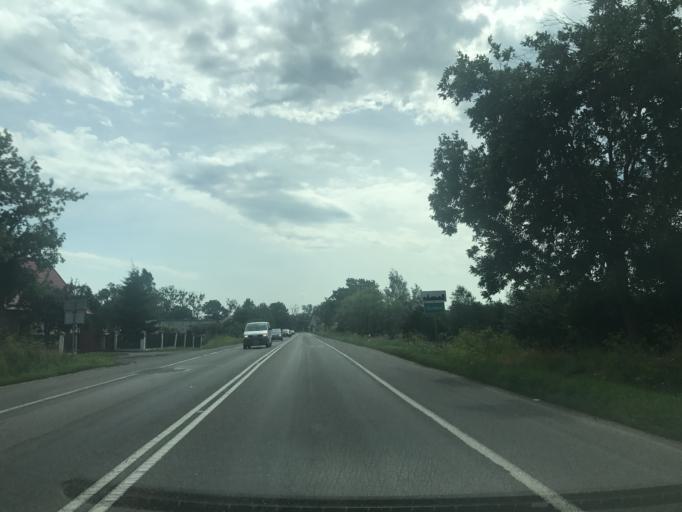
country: PL
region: Warmian-Masurian Voivodeship
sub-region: Powiat ostrodzki
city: Ostroda
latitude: 53.6505
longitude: 20.0514
